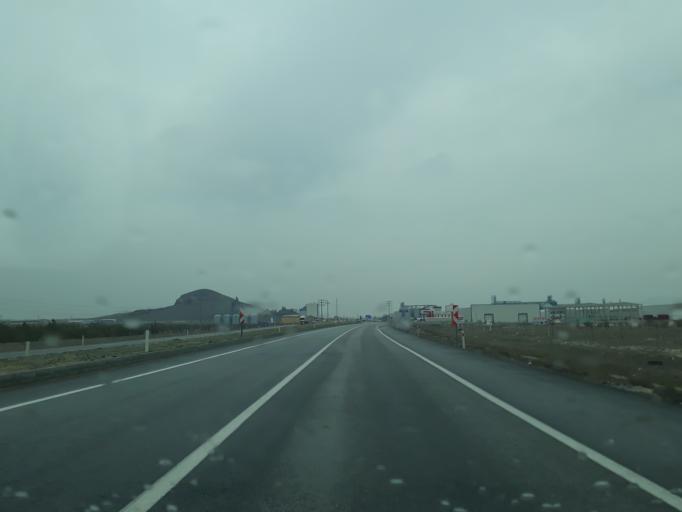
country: TR
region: Konya
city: Karapinar
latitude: 37.7134
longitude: 33.5968
